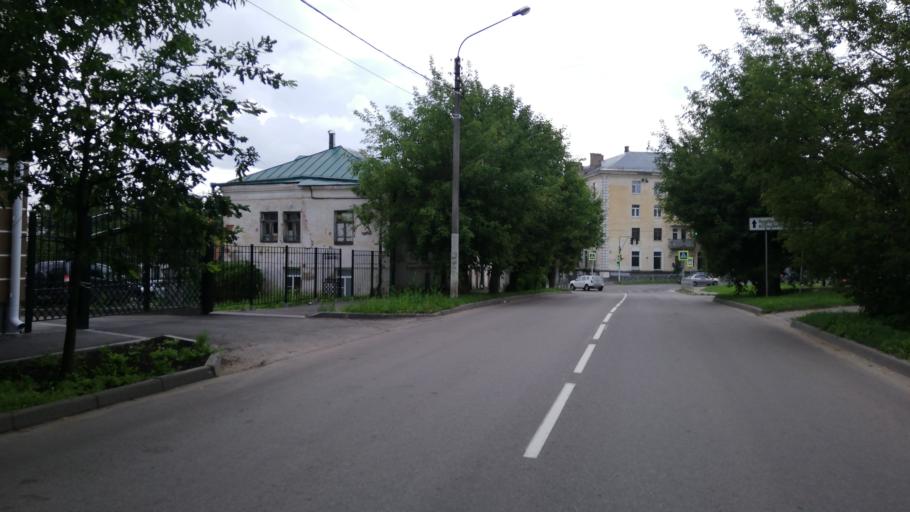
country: RU
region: Kostroma
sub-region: Kostromskoy Rayon
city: Kostroma
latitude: 57.7703
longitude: 40.9194
